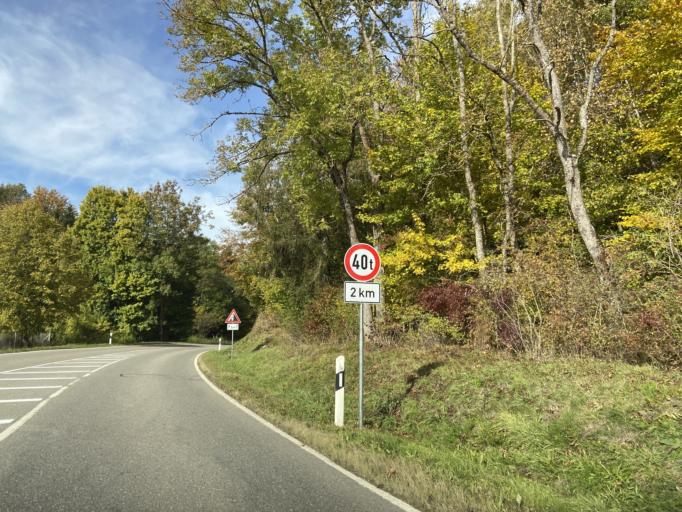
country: DE
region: Baden-Wuerttemberg
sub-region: Tuebingen Region
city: Leibertingen
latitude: 48.0572
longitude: 9.0422
